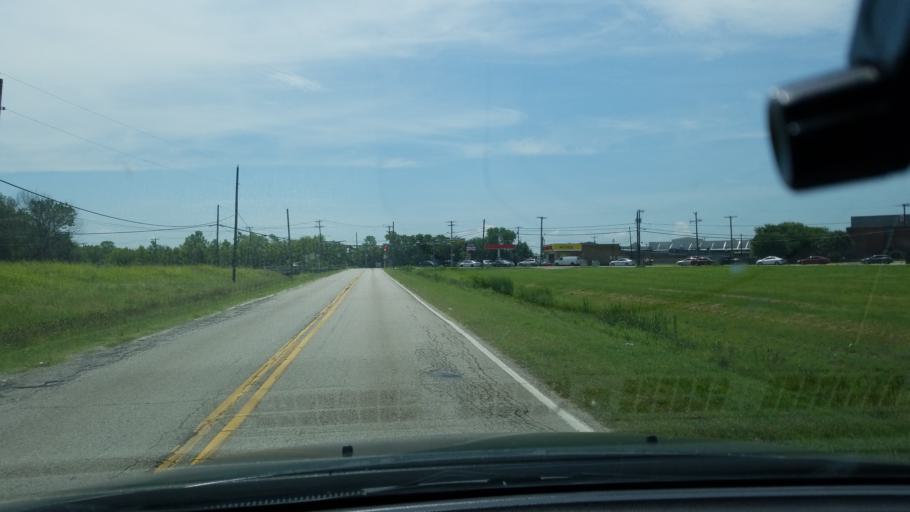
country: US
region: Texas
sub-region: Dallas County
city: Balch Springs
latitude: 32.7498
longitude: -96.6325
